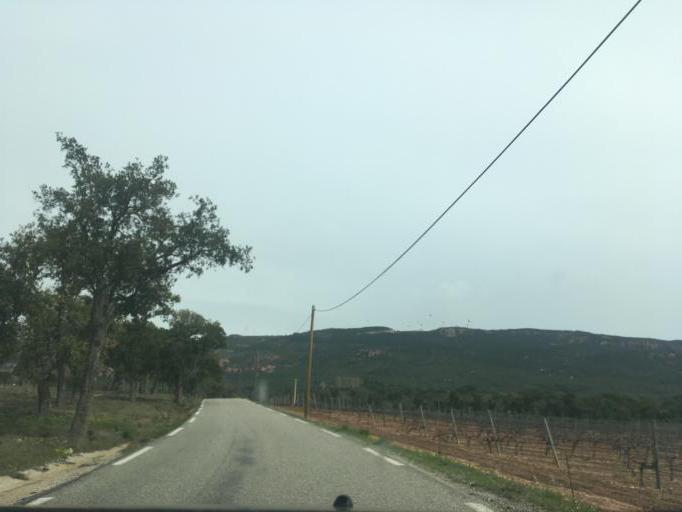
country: FR
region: Provence-Alpes-Cote d'Azur
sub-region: Departement du Var
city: Le Muy
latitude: 43.5100
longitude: 6.6133
